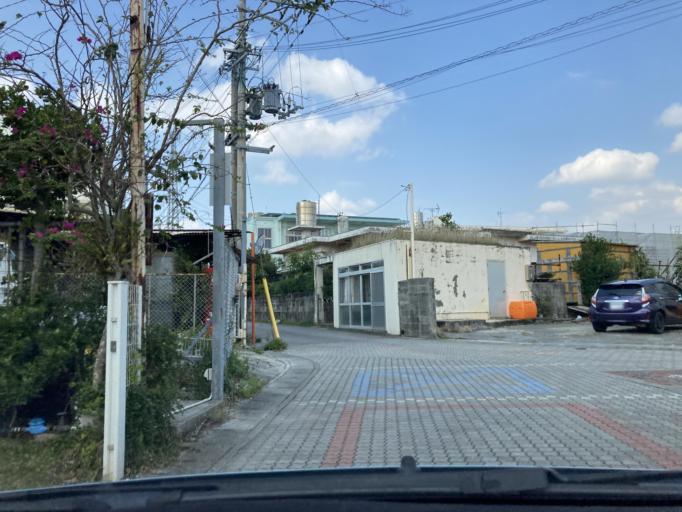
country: JP
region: Okinawa
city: Tomigusuku
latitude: 26.1878
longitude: 127.7241
